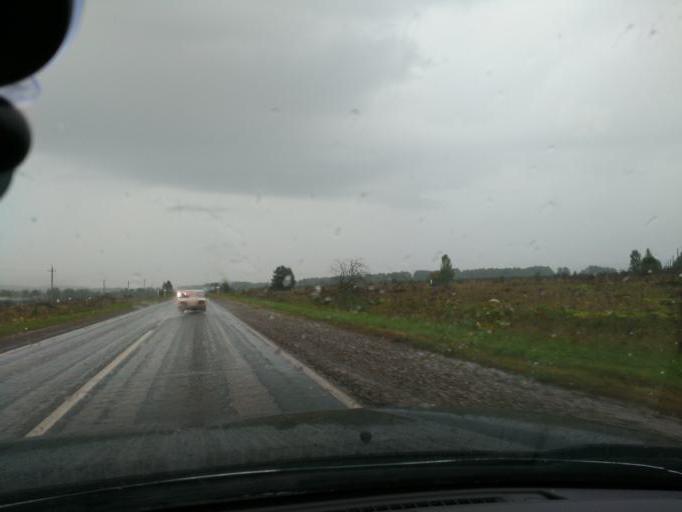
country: RU
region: Perm
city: Osa
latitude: 57.1386
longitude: 55.5276
